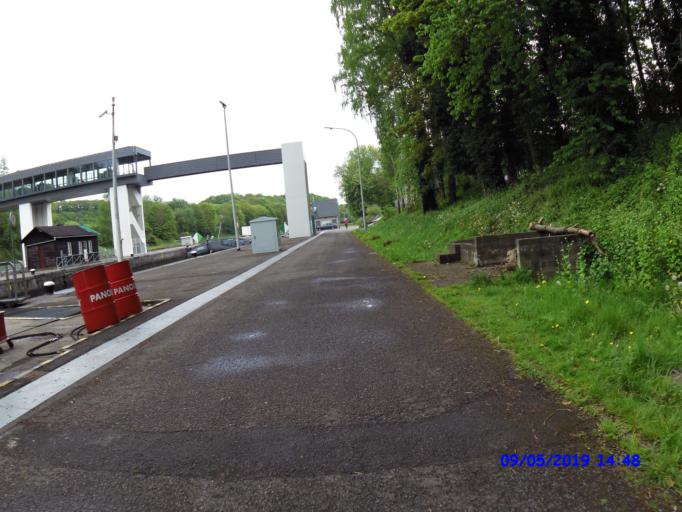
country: BE
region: Wallonia
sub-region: Province du Hainaut
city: Aiseau
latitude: 50.4535
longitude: 4.6264
